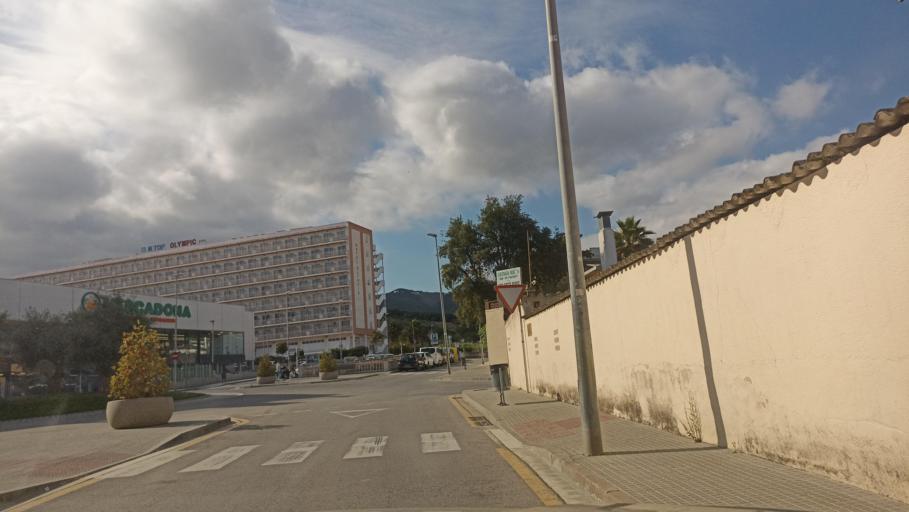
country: ES
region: Catalonia
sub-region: Provincia de Barcelona
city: Calella
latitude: 41.6142
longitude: 2.6533
